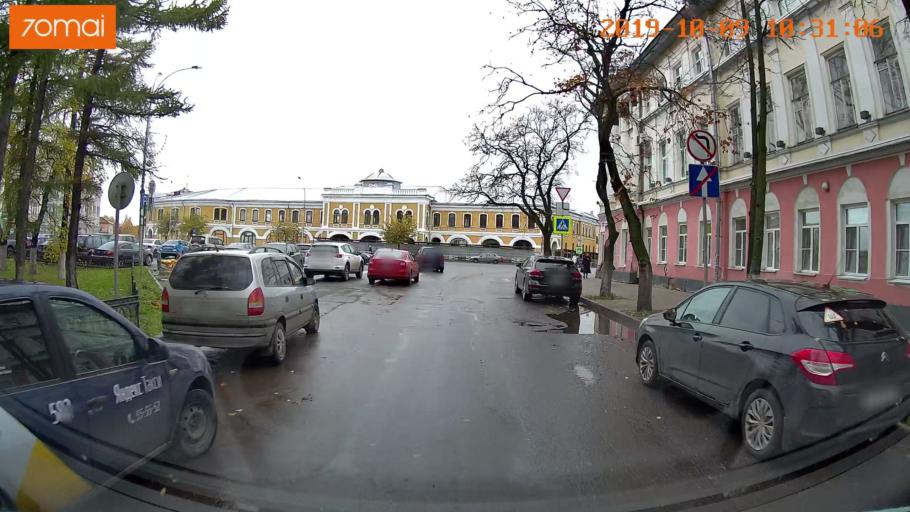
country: RU
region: Vologda
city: Vologda
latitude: 59.2208
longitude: 39.8934
